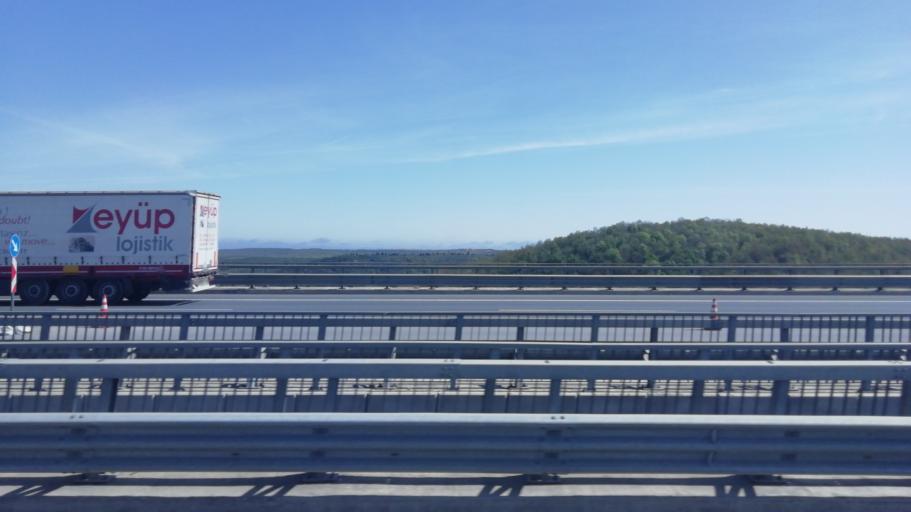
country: TR
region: Istanbul
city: Mahmut Sevket Pasa
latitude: 41.1814
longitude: 29.2334
